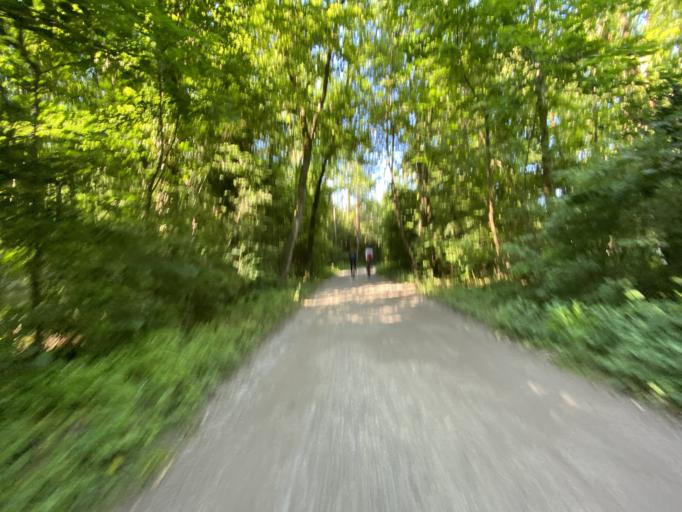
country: DE
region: Bavaria
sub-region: Upper Bavaria
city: Pasing
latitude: 48.1632
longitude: 11.4891
